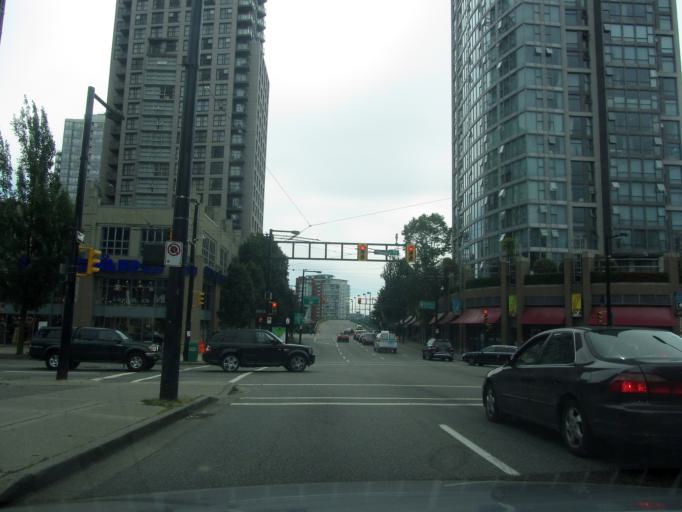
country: CA
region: British Columbia
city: Vancouver
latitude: 49.2710
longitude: -123.1148
